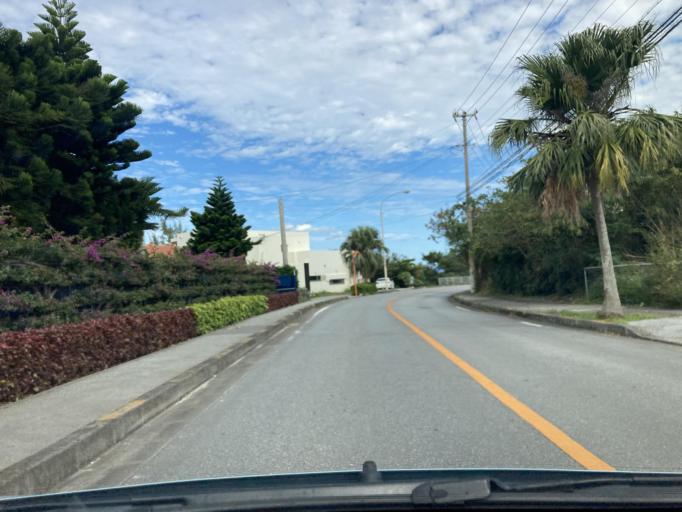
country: JP
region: Okinawa
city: Ishikawa
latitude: 26.4303
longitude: 127.7542
